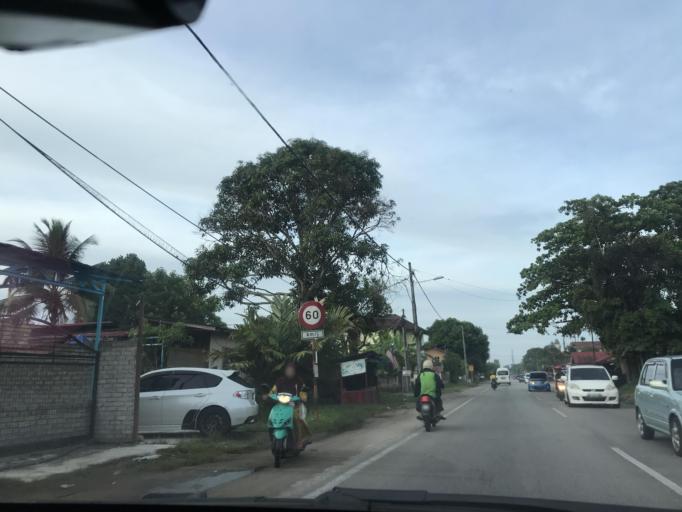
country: MY
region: Kelantan
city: Kota Bharu
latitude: 6.1028
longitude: 102.2110
